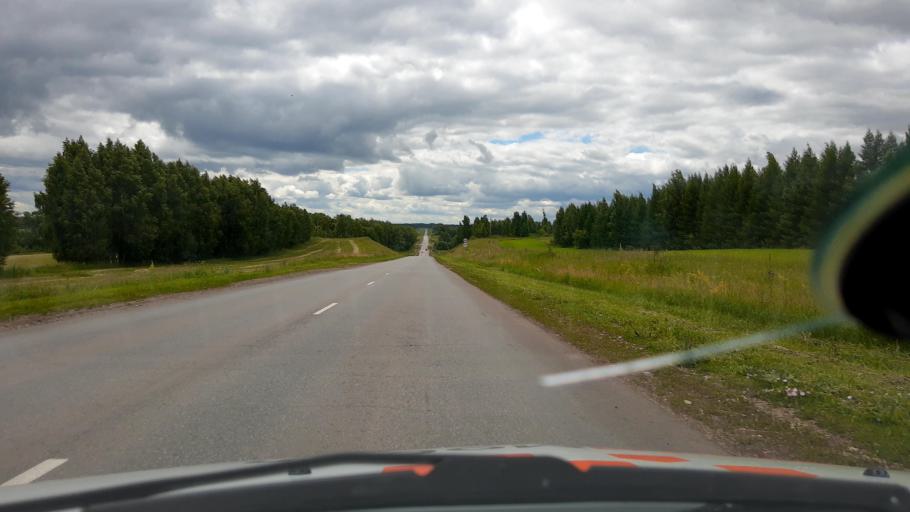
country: RU
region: Bashkortostan
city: Buzdyak
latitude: 54.6956
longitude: 54.5595
